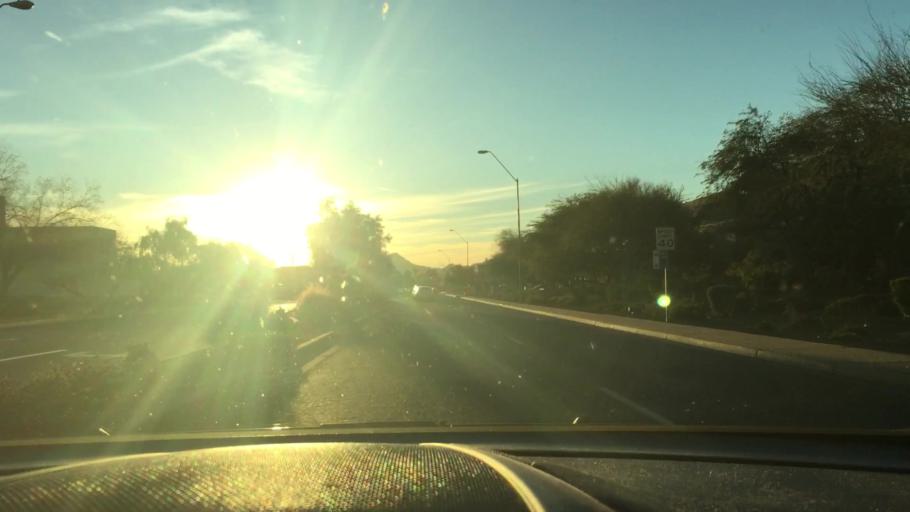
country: US
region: Arizona
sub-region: Maricopa County
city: Scottsdale
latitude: 33.5700
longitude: -111.8839
